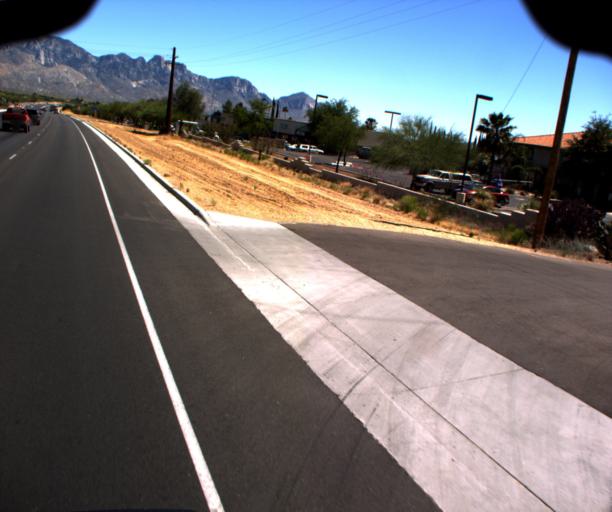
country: US
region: Arizona
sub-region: Pima County
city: Catalina
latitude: 32.4918
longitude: -110.9252
